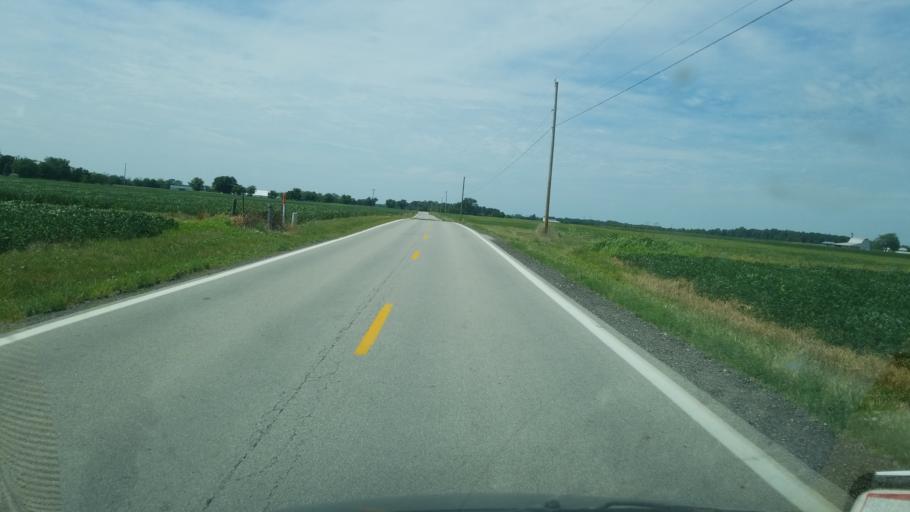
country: US
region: Ohio
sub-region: Madison County
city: West Jefferson
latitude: 39.8775
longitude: -83.3191
